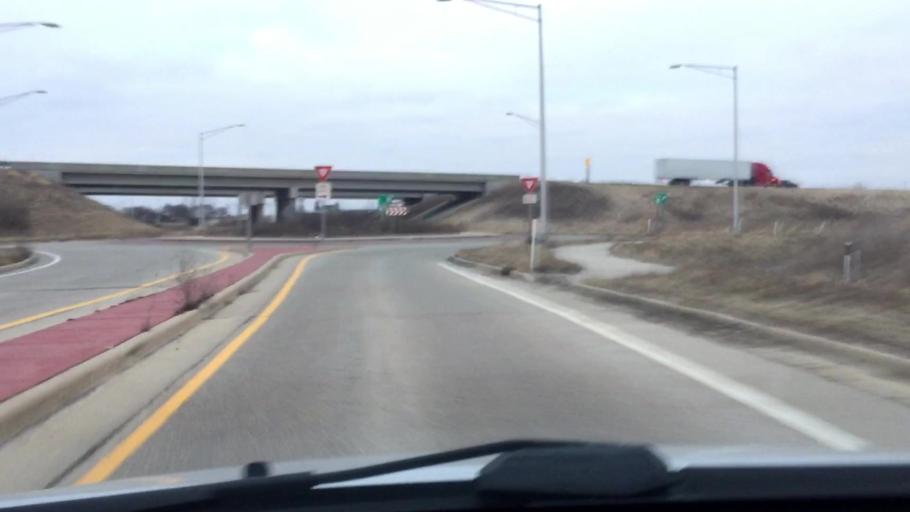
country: US
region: Wisconsin
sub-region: Jefferson County
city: Watertown
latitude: 43.1541
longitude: -88.7428
